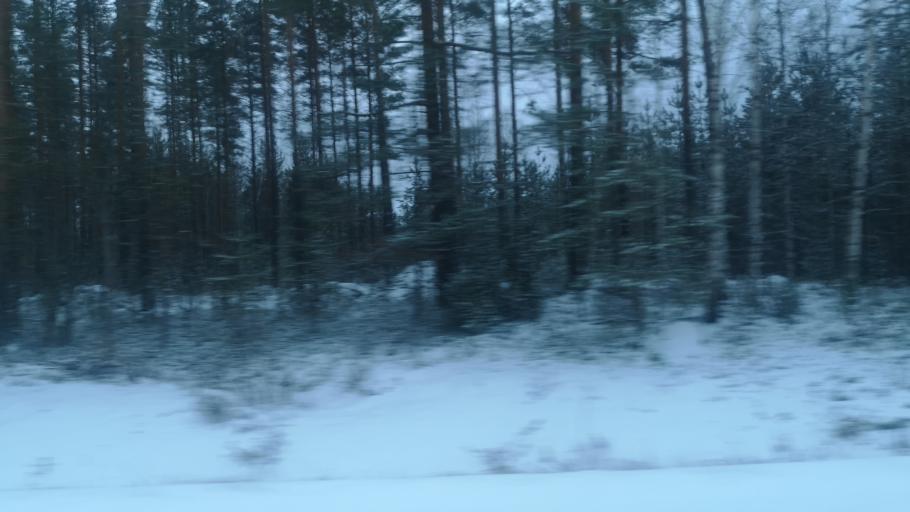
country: FI
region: Southern Savonia
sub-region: Savonlinna
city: Rantasalmi
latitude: 62.1101
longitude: 28.6138
